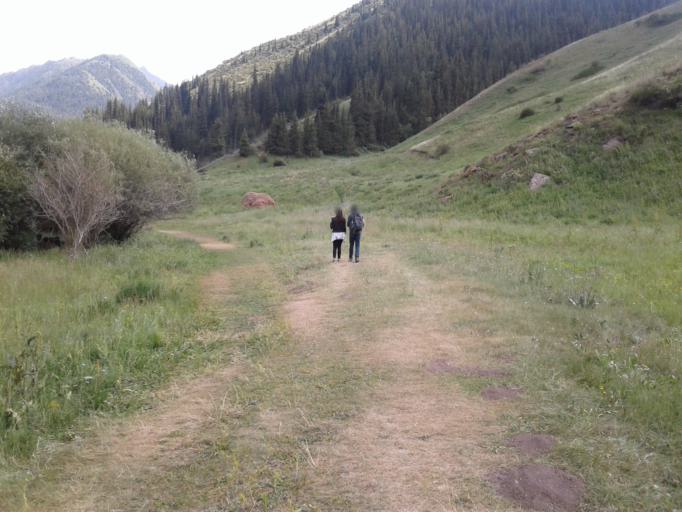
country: KG
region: Naryn
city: Naryn
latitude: 41.4580
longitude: 76.4527
